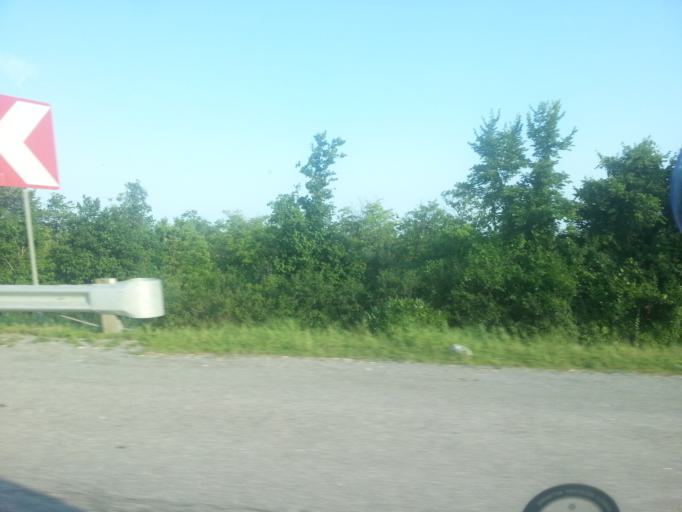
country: CA
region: Quebec
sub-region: Outaouais
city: Gatineau
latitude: 45.4476
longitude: -75.7199
